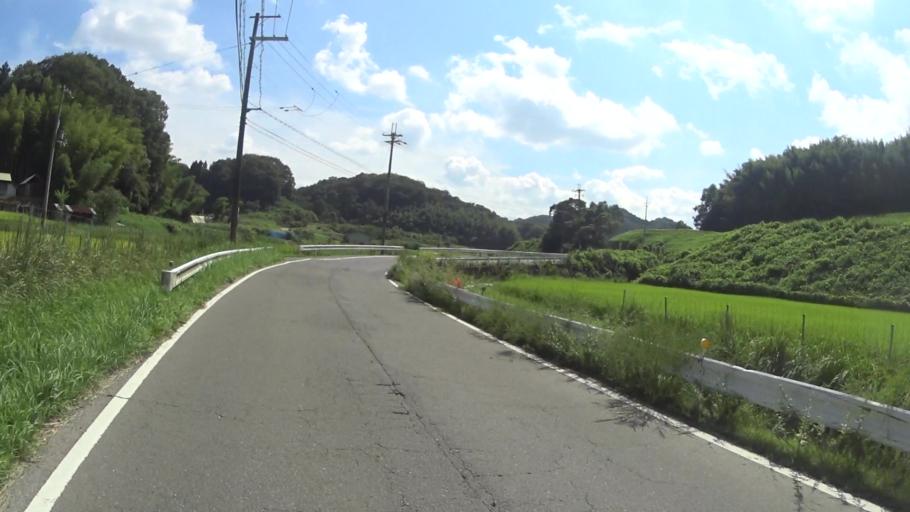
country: JP
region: Kyoto
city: Tanabe
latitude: 34.7693
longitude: 135.7488
